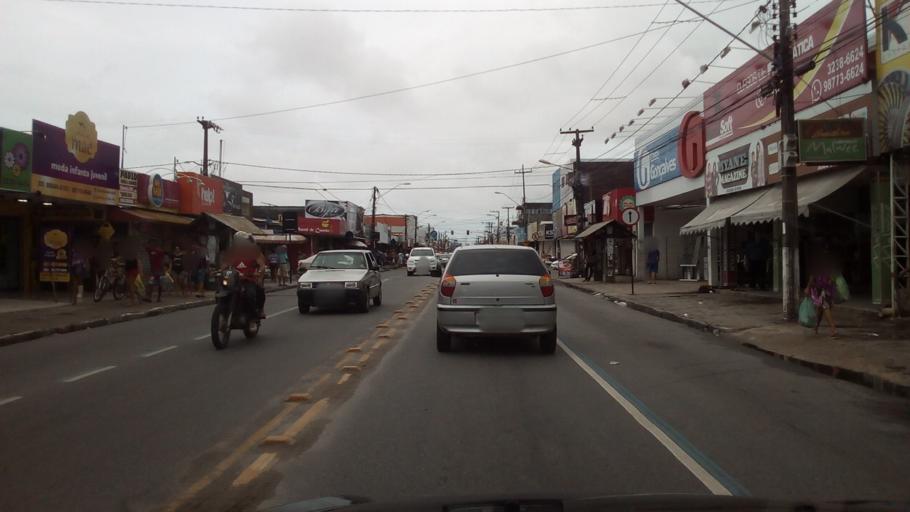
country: BR
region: Paraiba
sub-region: Joao Pessoa
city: Joao Pessoa
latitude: -7.1679
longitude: -34.8385
